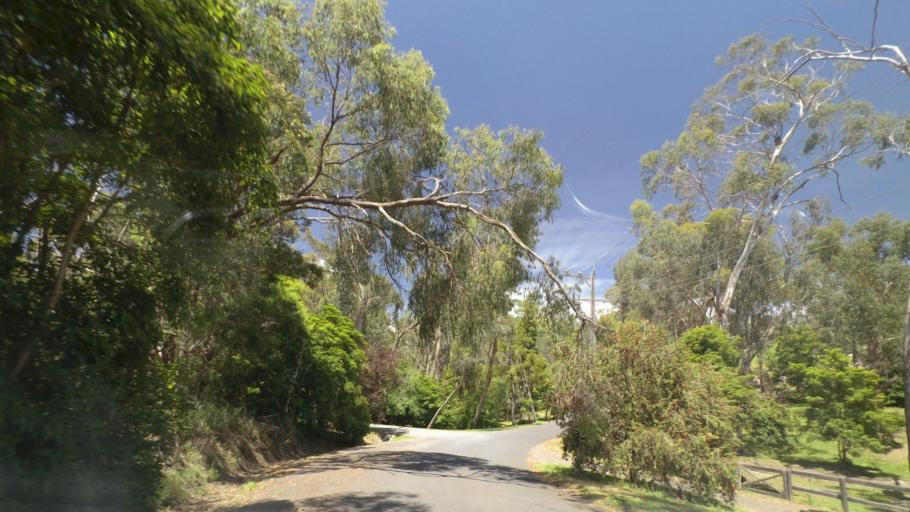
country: AU
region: Victoria
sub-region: Yarra Ranges
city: Chirnside Park
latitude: -37.7507
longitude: 145.2854
